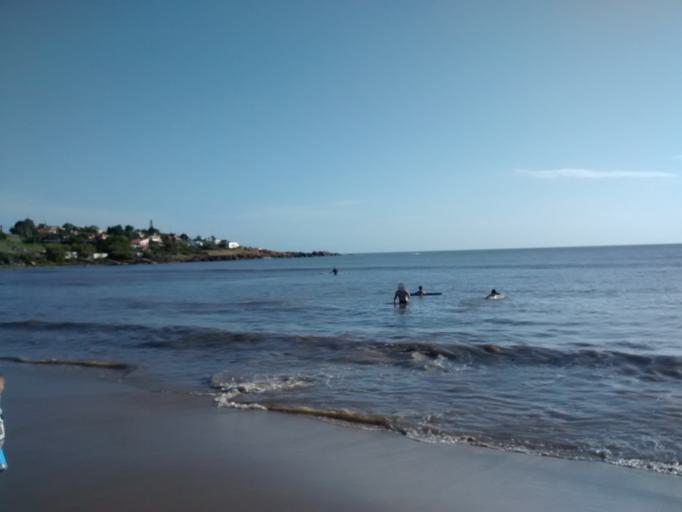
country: UY
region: Maldonado
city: Piriapolis
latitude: -34.8953
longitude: -55.2601
